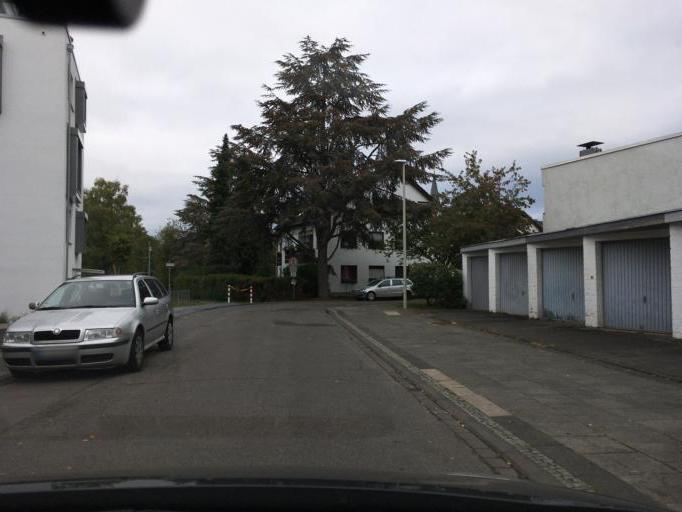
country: DE
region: North Rhine-Westphalia
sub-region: Regierungsbezirk Koln
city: Bonn
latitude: 50.7483
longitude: 7.1140
